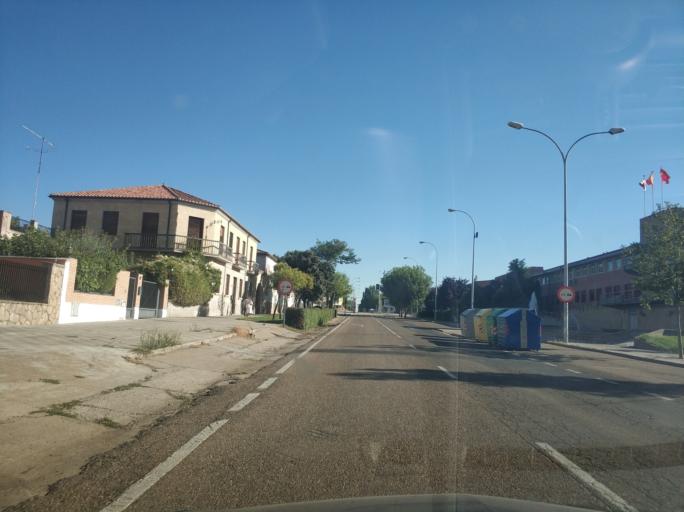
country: ES
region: Castille and Leon
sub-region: Provincia de Salamanca
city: Salamanca
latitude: 40.9780
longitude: -5.6619
